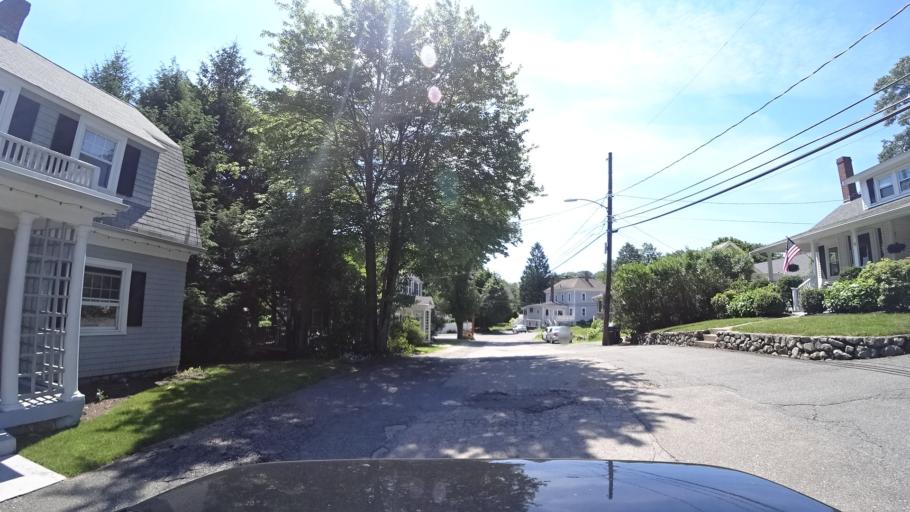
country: US
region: Massachusetts
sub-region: Norfolk County
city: Dedham
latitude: 42.2433
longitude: -71.1580
